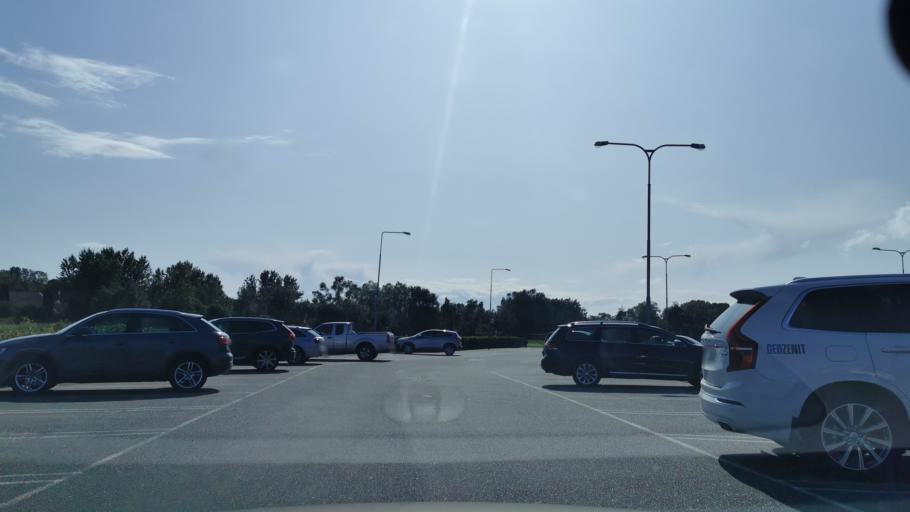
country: SE
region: Vaestra Goetaland
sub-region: Goteborg
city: Majorna
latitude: 57.6415
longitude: 11.9257
